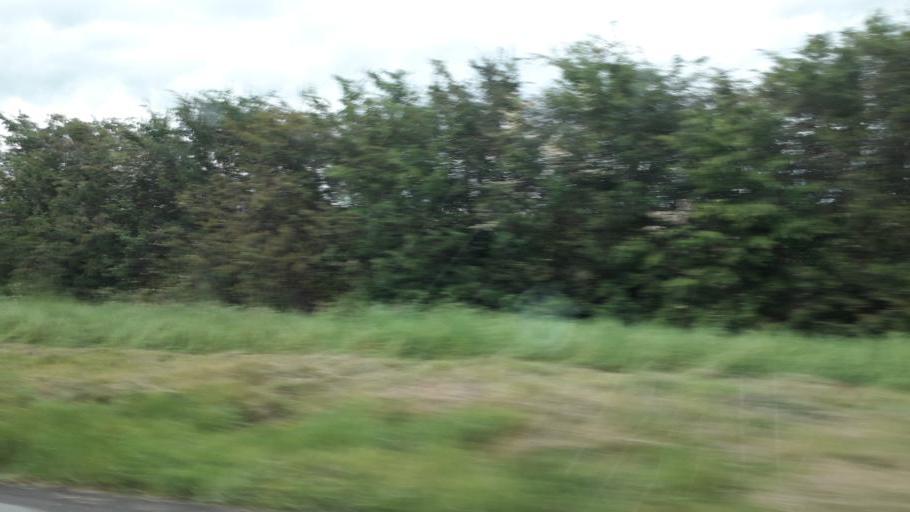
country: IE
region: Leinster
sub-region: County Carlow
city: Bagenalstown
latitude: 52.7334
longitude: -6.9863
